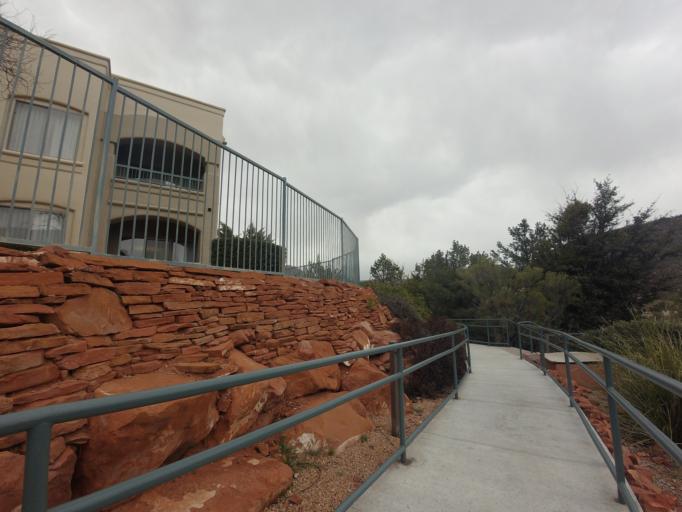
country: US
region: Arizona
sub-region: Yavapai County
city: Big Park
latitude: 34.7712
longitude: -111.7678
